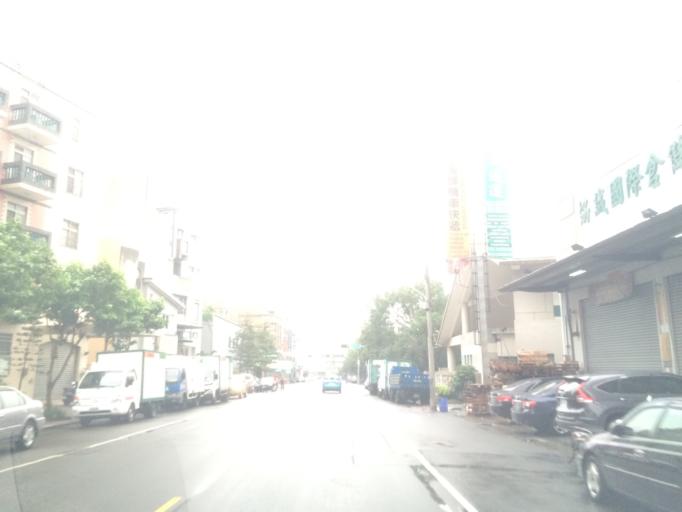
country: TW
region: Taiwan
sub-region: Taichung City
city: Taichung
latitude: 24.1847
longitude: 120.6872
